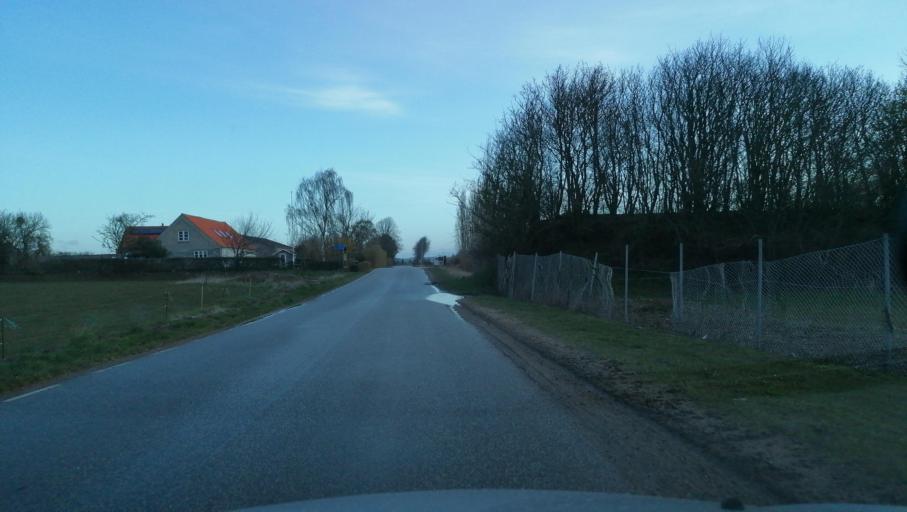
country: DK
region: Zealand
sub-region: Odsherred Kommune
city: Horve
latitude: 55.7579
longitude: 11.4400
